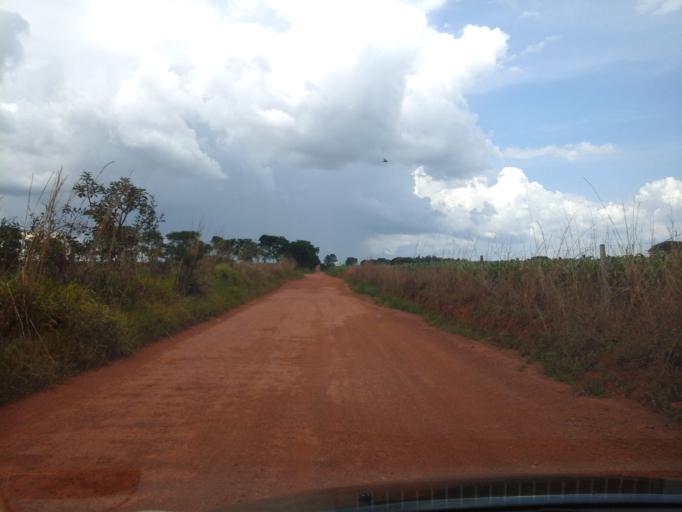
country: BR
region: Goias
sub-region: Abadiania
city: Abadiania
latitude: -15.9929
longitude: -48.5375
